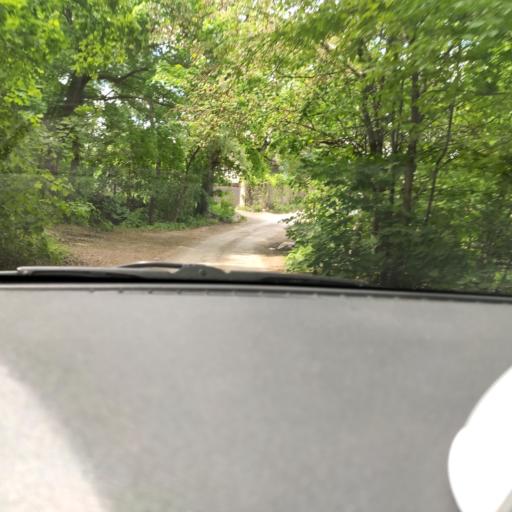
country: RU
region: Samara
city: Petra-Dubrava
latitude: 53.3017
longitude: 50.2357
